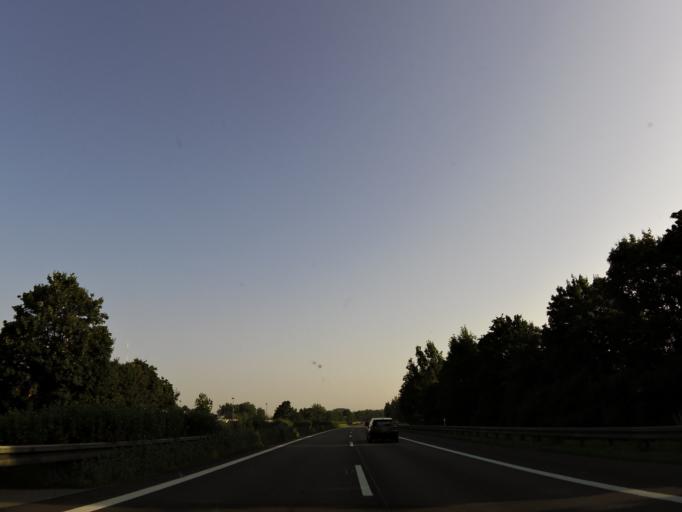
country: DE
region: Bavaria
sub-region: Swabia
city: Kellmunz
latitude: 48.1237
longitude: 10.1113
